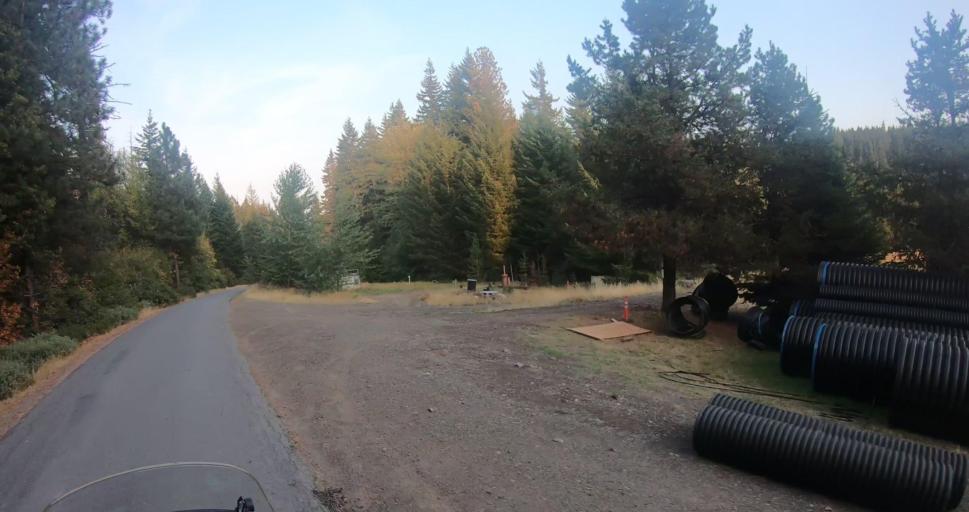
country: US
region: Oregon
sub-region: Hood River County
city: Odell
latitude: 45.4647
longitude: -121.6253
